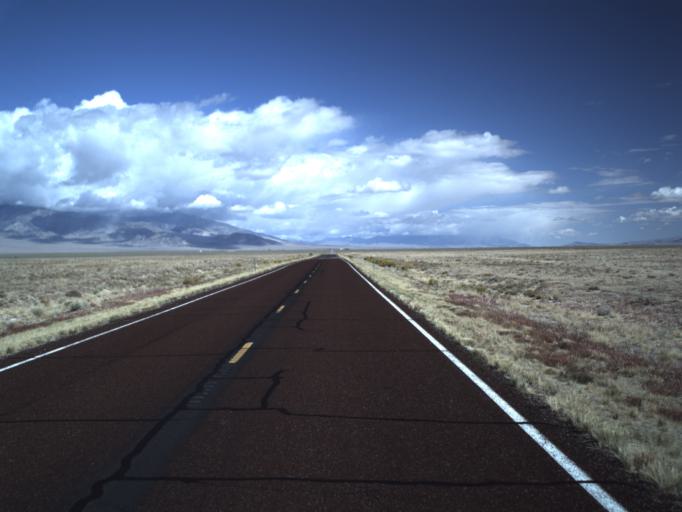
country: US
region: Nevada
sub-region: White Pine County
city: McGill
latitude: 38.9727
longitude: -114.0339
